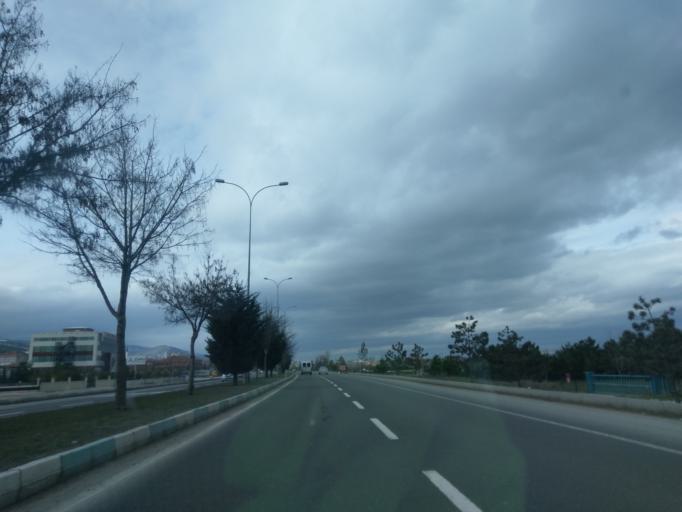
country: TR
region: Kuetahya
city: Kutahya
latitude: 39.4102
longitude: 30.0210
